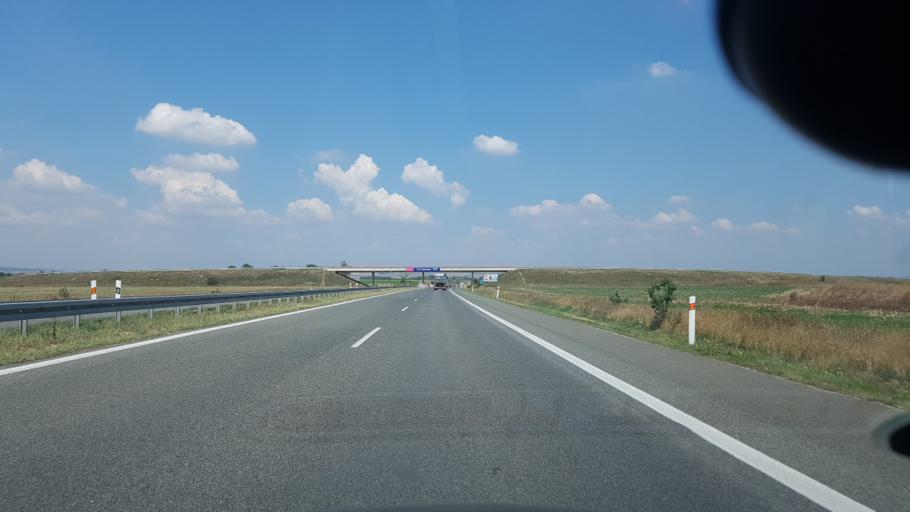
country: CZ
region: South Moravian
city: Hrusovany u Brna
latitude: 49.0362
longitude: 16.5439
